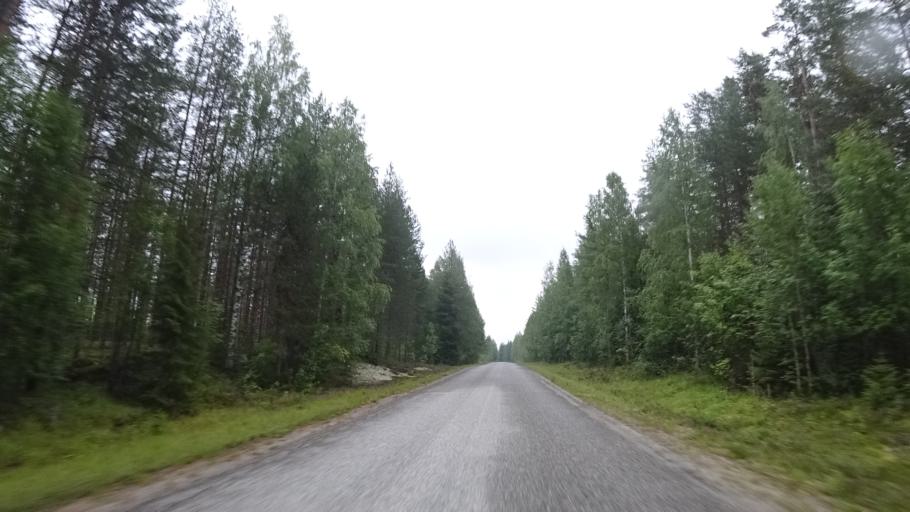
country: FI
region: North Karelia
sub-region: Joensuu
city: Ilomantsi
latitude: 63.2281
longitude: 30.8230
